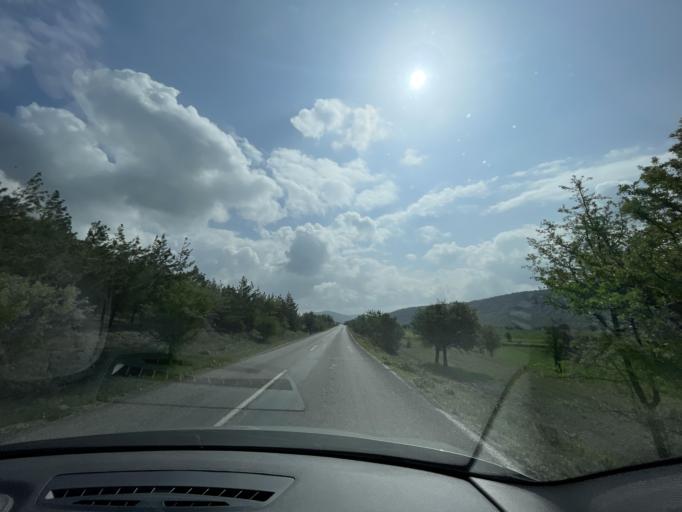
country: TR
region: Denizli
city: Acipayam
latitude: 37.5106
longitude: 29.4484
